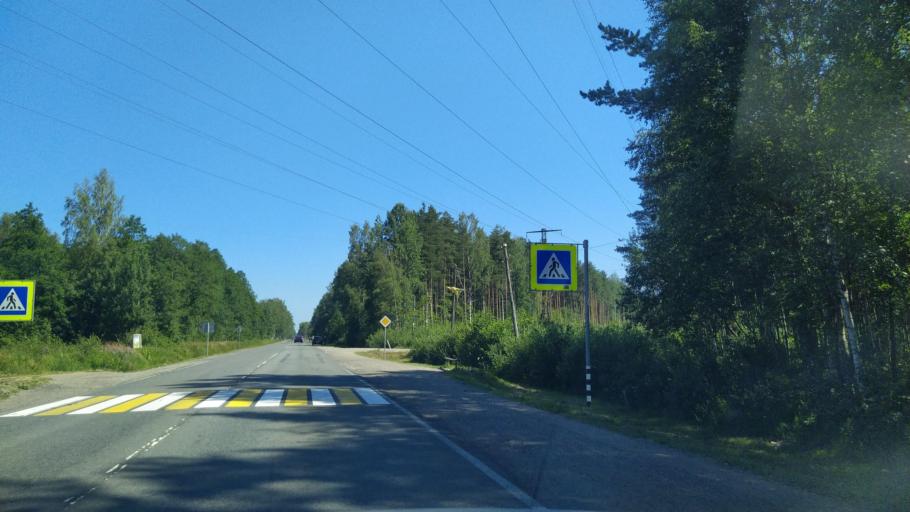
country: RU
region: Leningrad
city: Imeni Morozova
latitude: 59.9623
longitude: 31.0090
